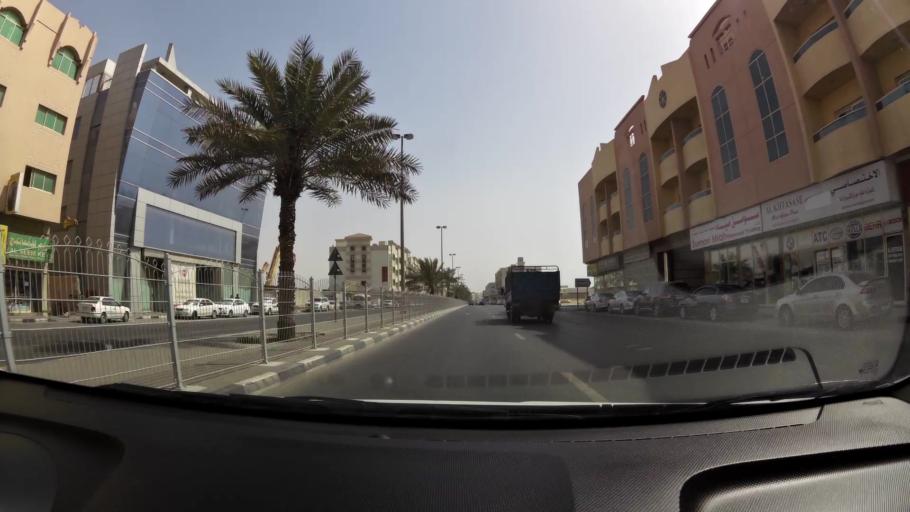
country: AE
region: Ash Shariqah
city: Sharjah
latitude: 25.3138
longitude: 55.4244
